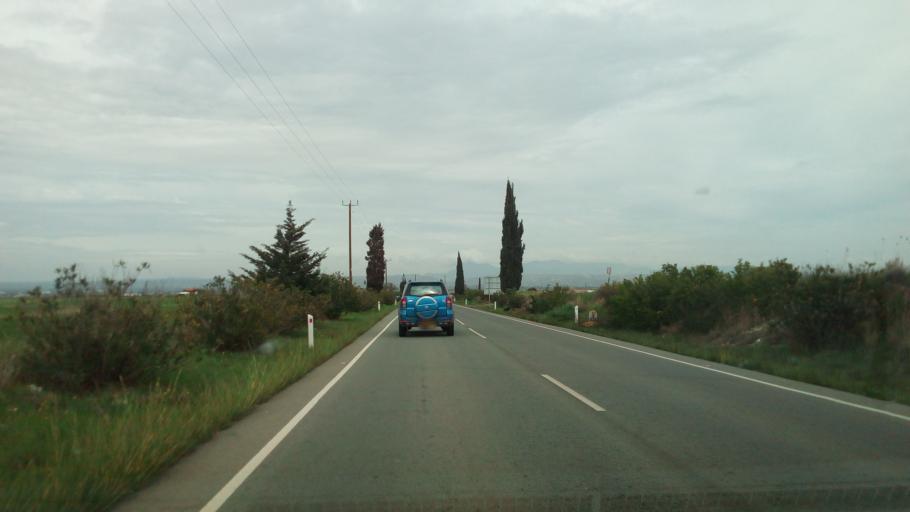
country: CY
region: Lefkosia
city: Astromeritis
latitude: 35.1229
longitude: 33.0102
